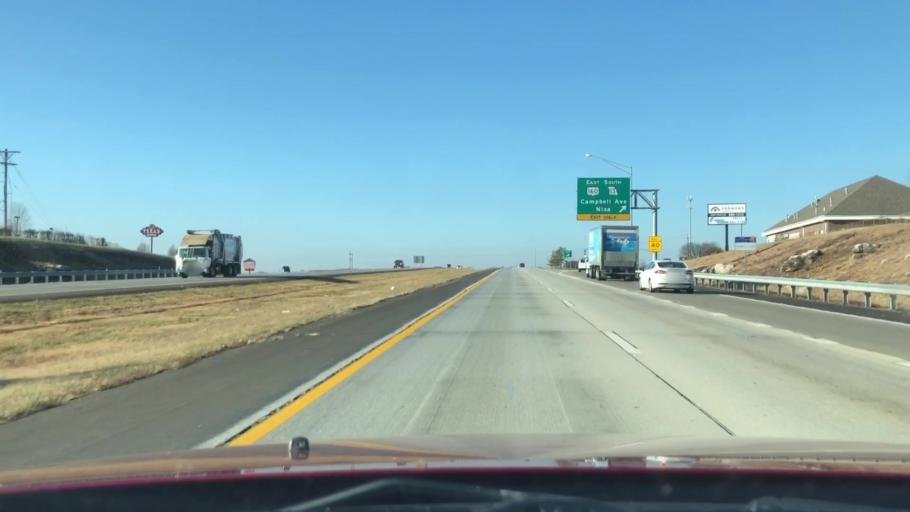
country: US
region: Missouri
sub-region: Greene County
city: Springfield
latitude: 37.1380
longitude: -93.2913
